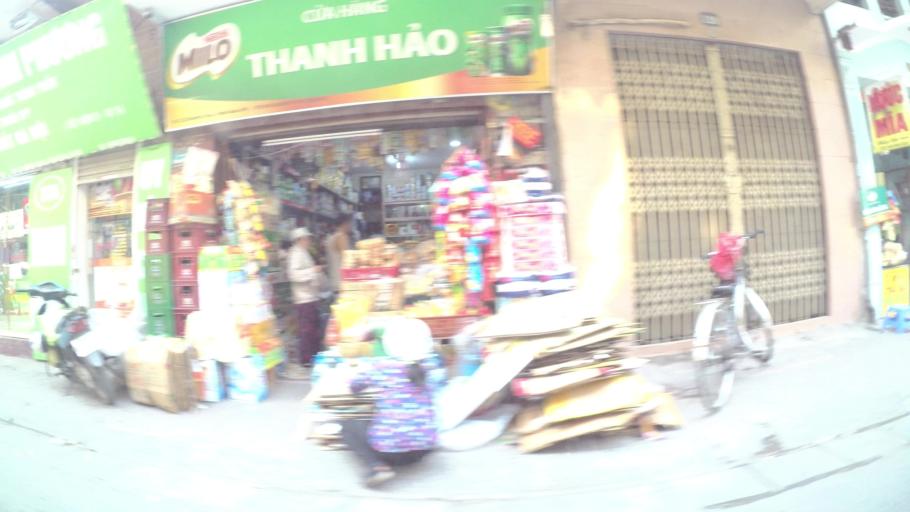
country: VN
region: Ha Noi
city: Thanh Xuan
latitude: 20.9974
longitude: 105.8182
